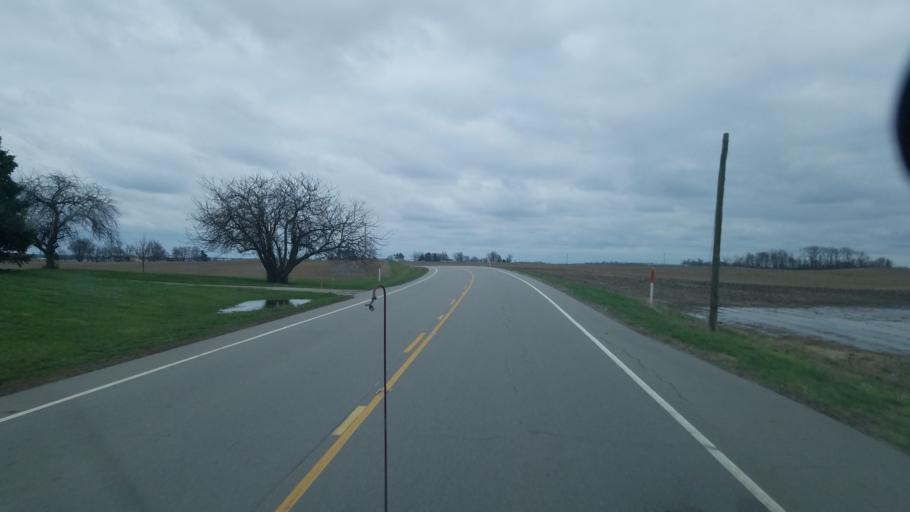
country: US
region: Ohio
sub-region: Fayette County
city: Washington Court House
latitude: 39.5730
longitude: -83.5121
